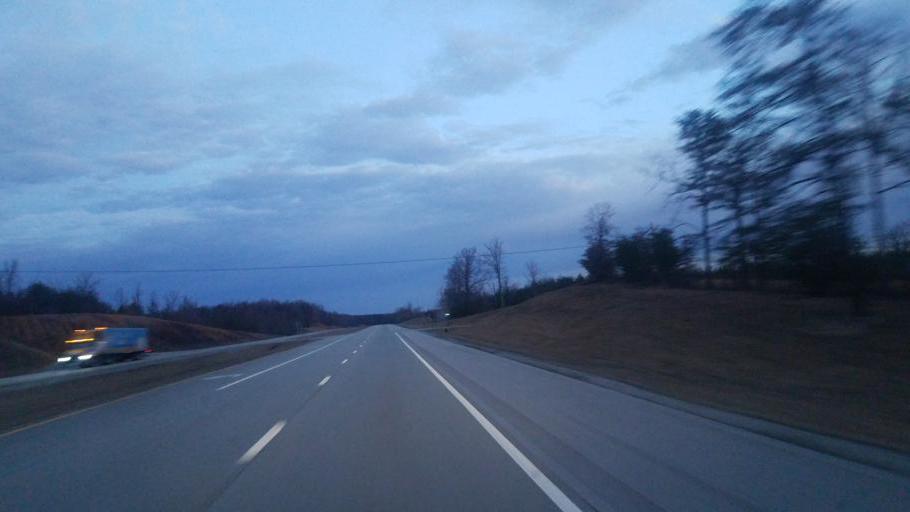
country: US
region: Tennessee
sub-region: Van Buren County
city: Spencer
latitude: 35.6817
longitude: -85.4767
